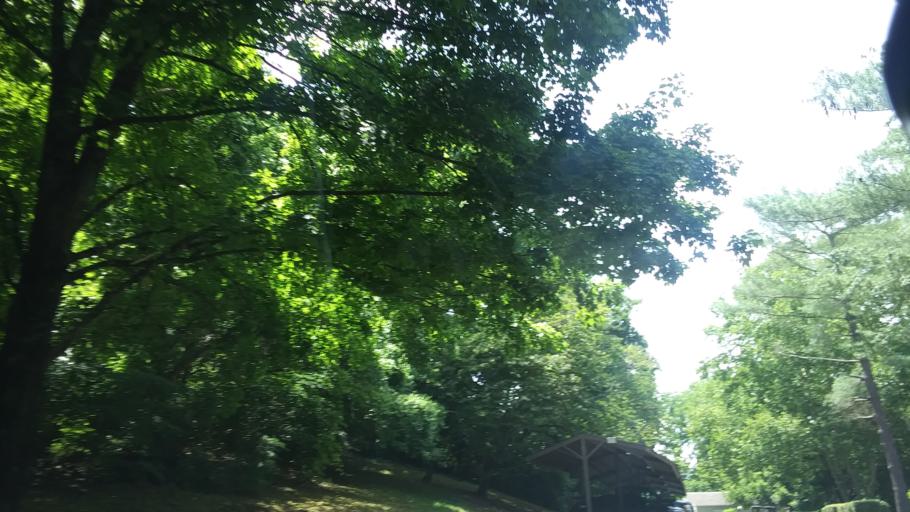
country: US
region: Tennessee
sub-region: Rutherford County
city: La Vergne
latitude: 36.0900
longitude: -86.6444
